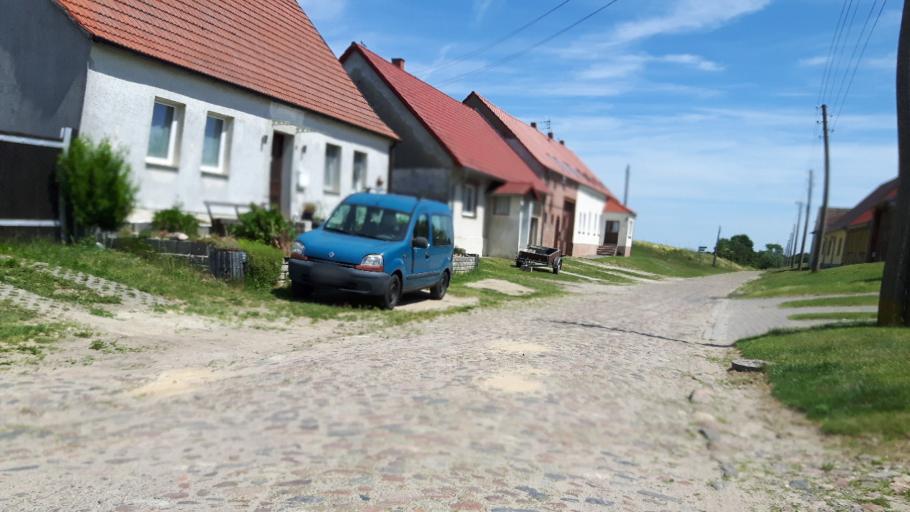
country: DE
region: Saxony-Anhalt
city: Kropstadt
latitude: 52.0068
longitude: 12.7240
